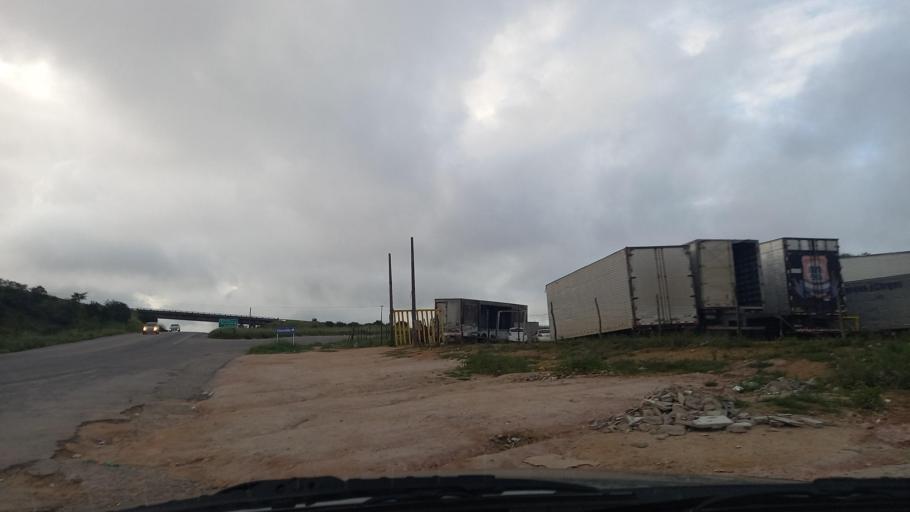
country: BR
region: Pernambuco
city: Garanhuns
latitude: -8.8793
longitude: -36.5069
